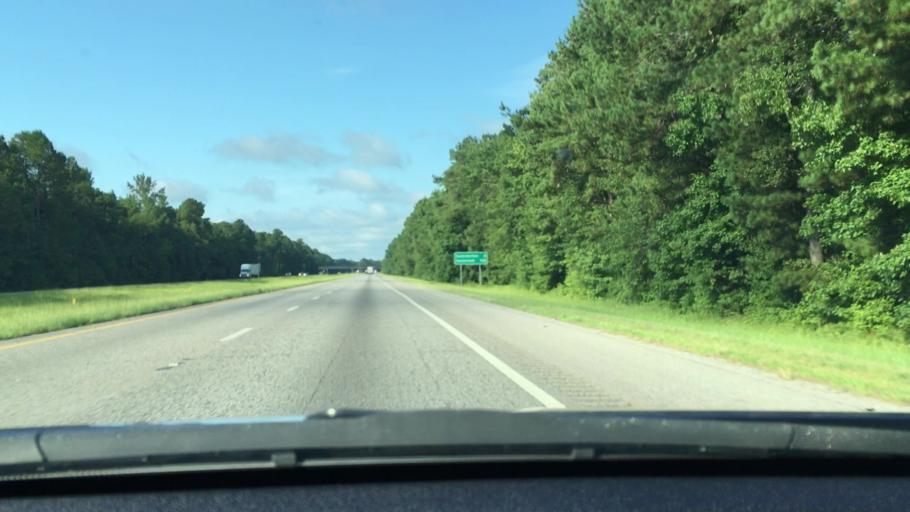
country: US
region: South Carolina
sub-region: Clarendon County
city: Manning
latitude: 33.6942
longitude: -80.2540
